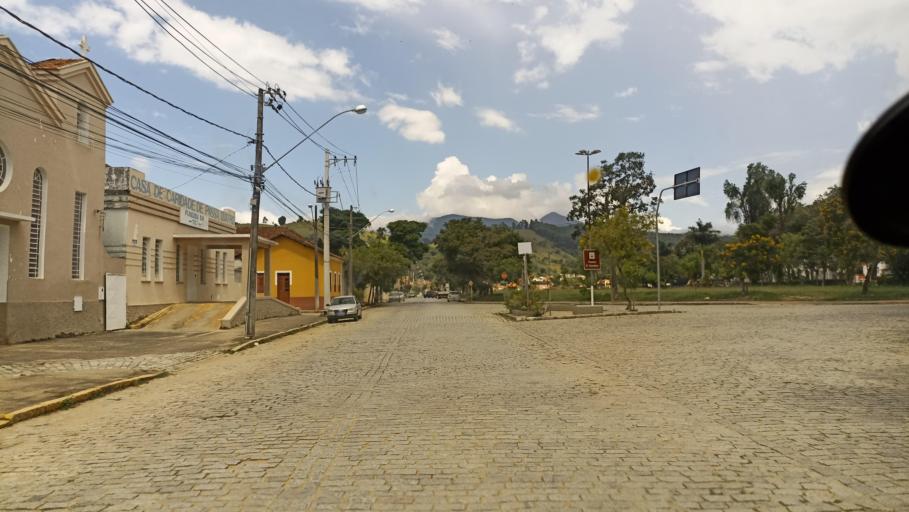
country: BR
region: Minas Gerais
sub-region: Passa Quatro
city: Passa Quatro
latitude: -22.3864
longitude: -44.9657
